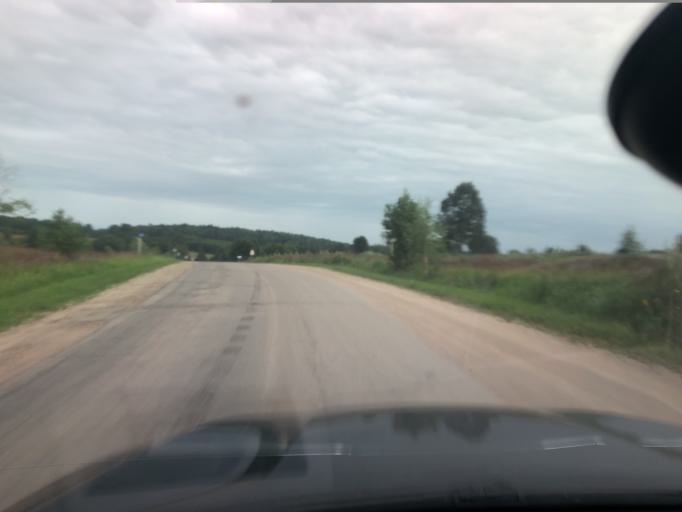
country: RU
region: Jaroslavl
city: Petrovsk
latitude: 56.9840
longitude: 39.1408
